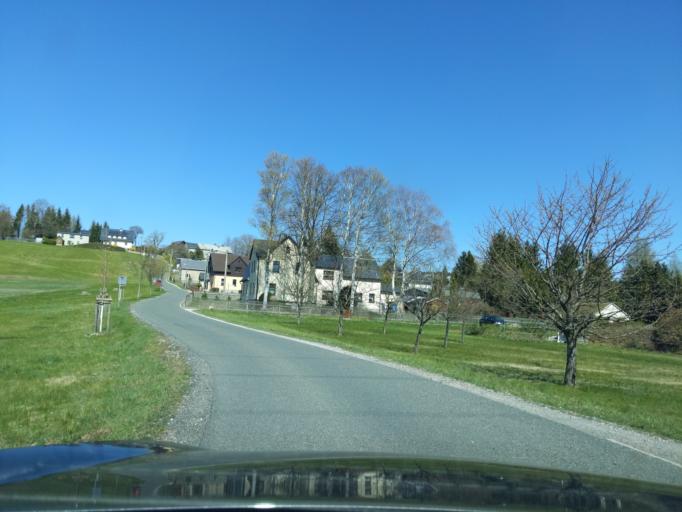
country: DE
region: Saxony
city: Schoenheide
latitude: 50.5095
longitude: 12.5419
